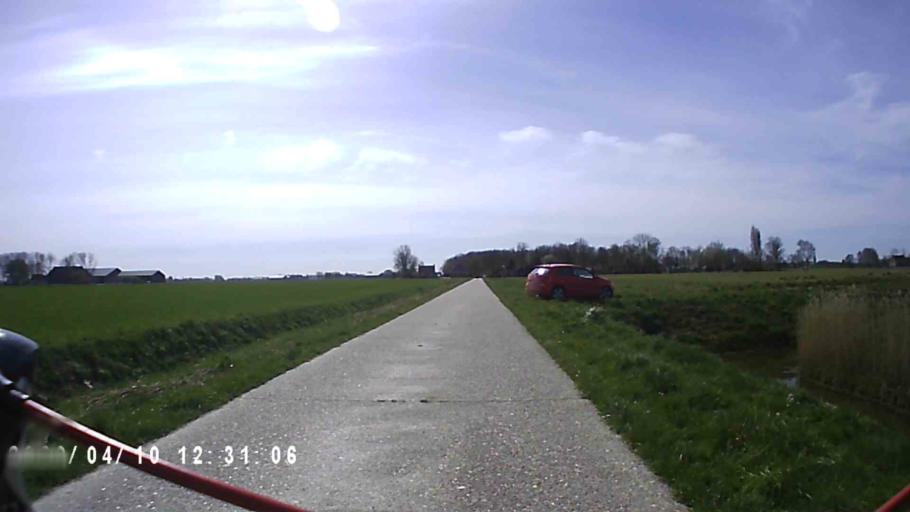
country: NL
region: Groningen
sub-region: Gemeente De Marne
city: Ulrum
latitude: 53.3983
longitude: 6.4096
